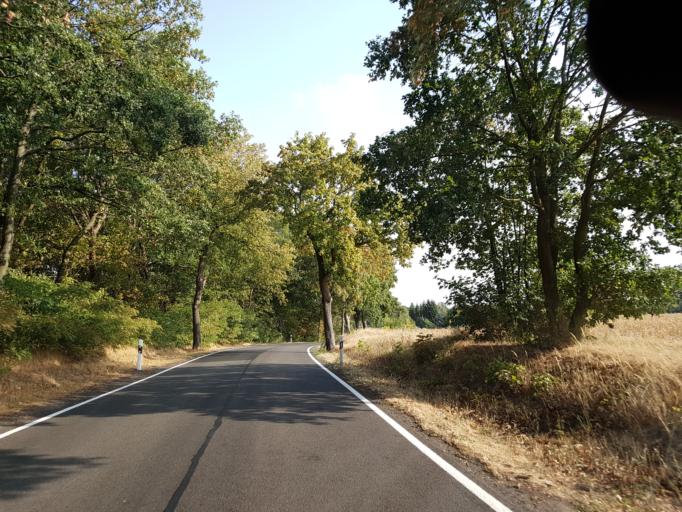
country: DE
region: Saxony-Anhalt
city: Pretzsch
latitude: 51.6777
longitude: 12.8292
